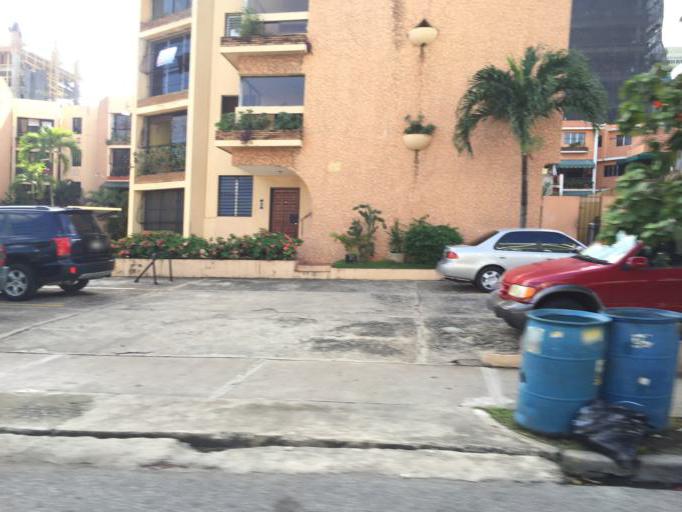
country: DO
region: Nacional
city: La Julia
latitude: 18.4796
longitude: -69.9382
